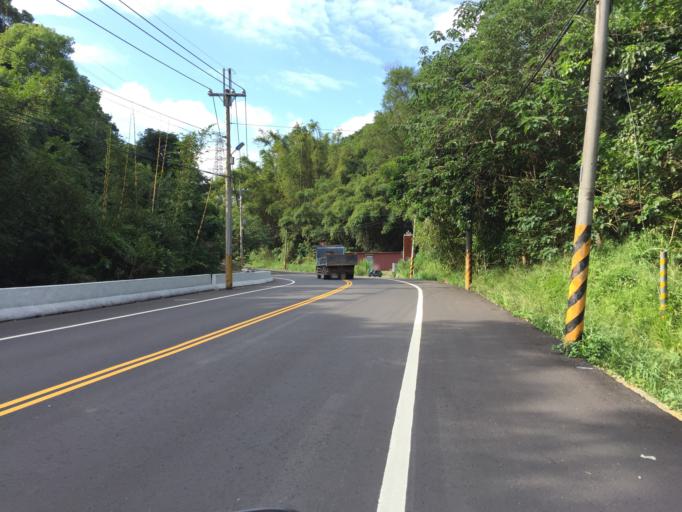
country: TW
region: Taiwan
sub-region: Hsinchu
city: Hsinchu
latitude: 24.7634
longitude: 120.9430
